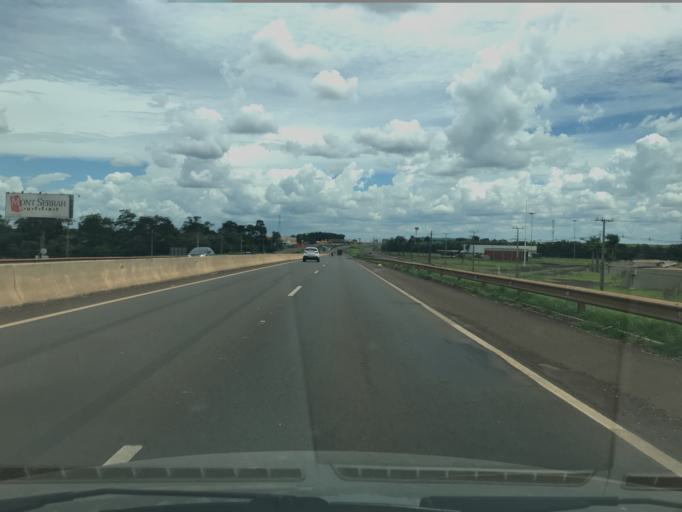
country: BR
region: Parana
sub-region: Paicandu
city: Paicandu
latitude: -23.4507
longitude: -52.0064
